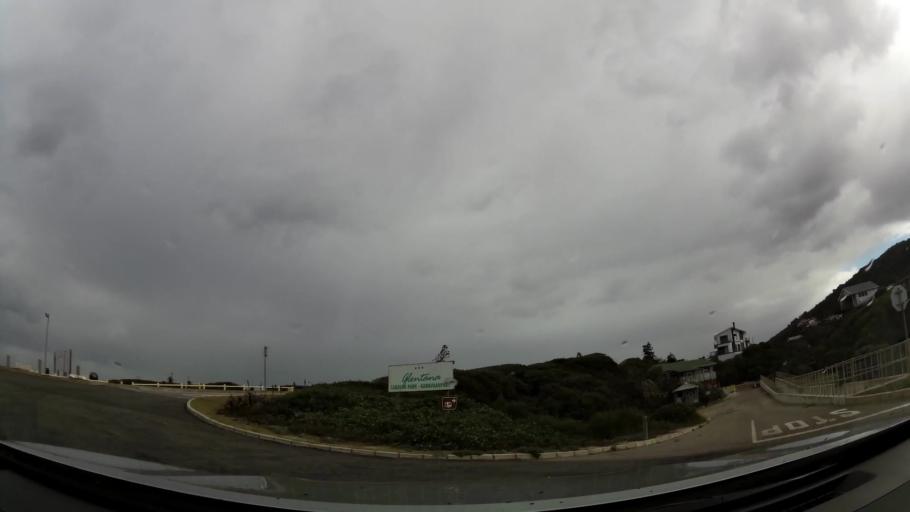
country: ZA
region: Western Cape
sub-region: Eden District Municipality
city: George
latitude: -34.0503
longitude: 22.3147
